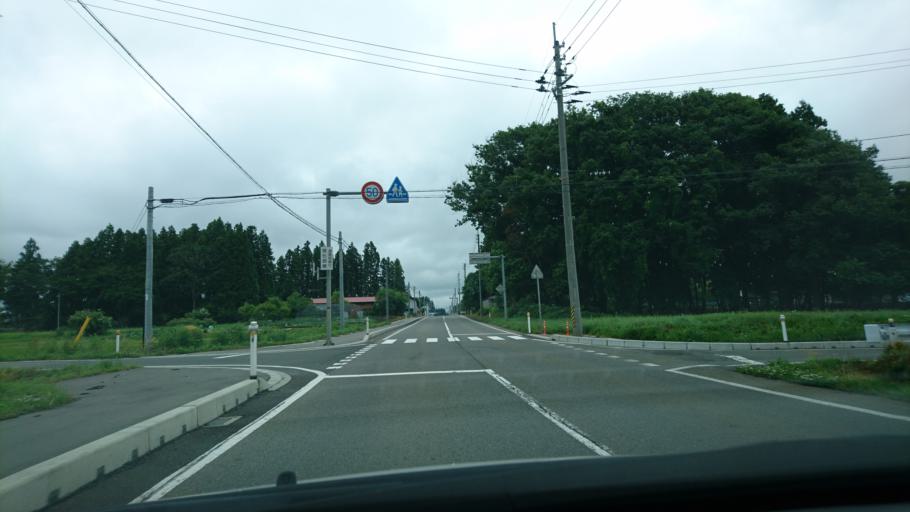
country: JP
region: Iwate
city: Mizusawa
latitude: 39.1028
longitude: 141.0515
